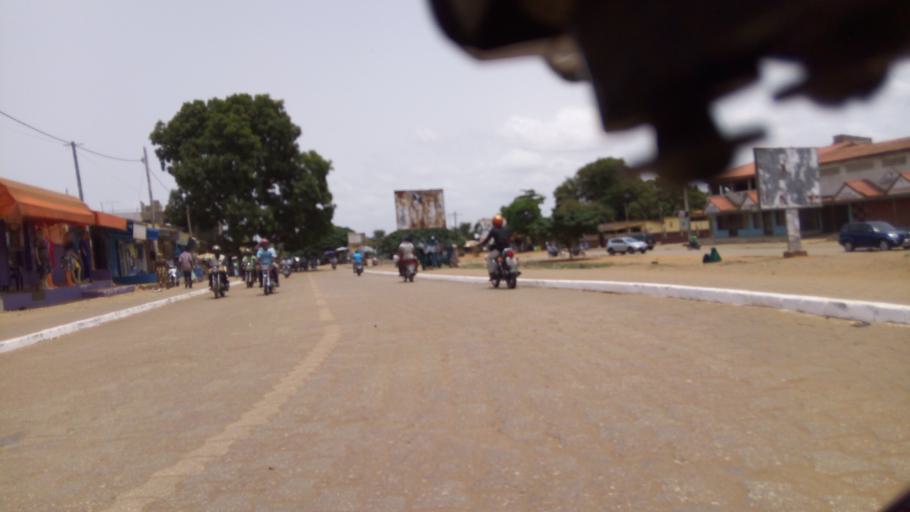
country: TG
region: Maritime
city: Lome
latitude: 6.1564
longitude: 1.2163
